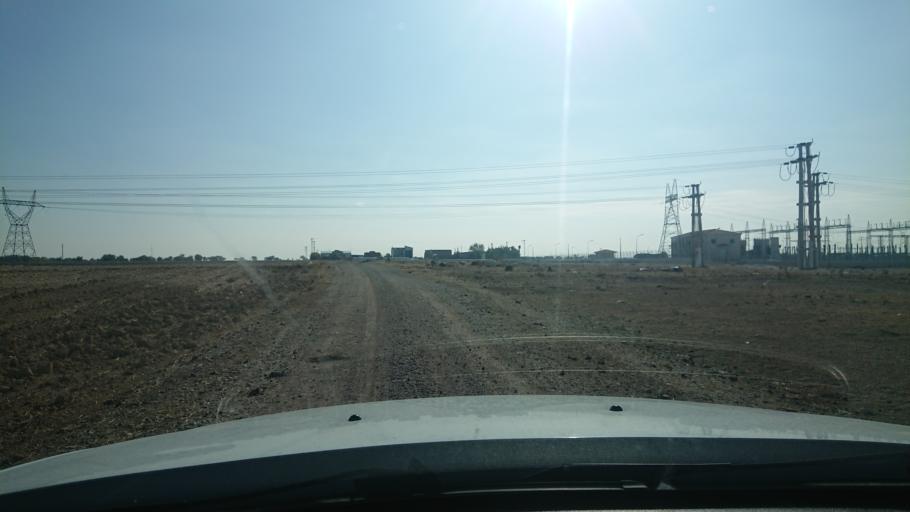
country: TR
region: Aksaray
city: Sultanhani
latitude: 38.2548
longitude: 33.4716
